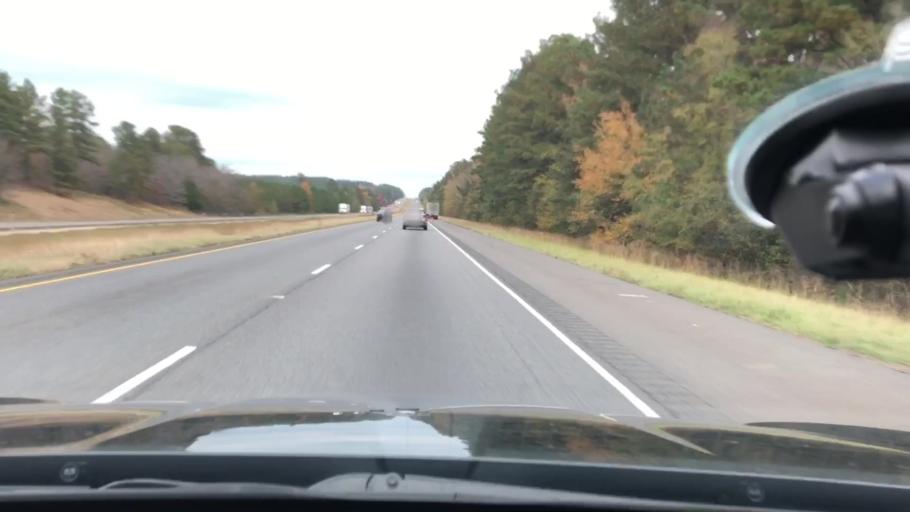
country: US
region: Arkansas
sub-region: Clark County
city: Arkadelphia
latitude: 34.2583
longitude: -92.9836
